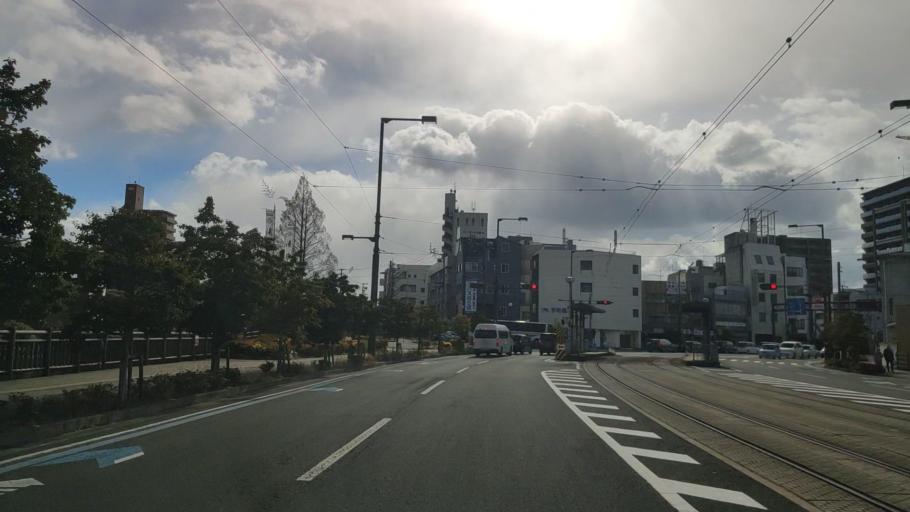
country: JP
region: Ehime
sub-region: Shikoku-chuo Shi
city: Matsuyama
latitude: 33.8488
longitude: 132.7851
